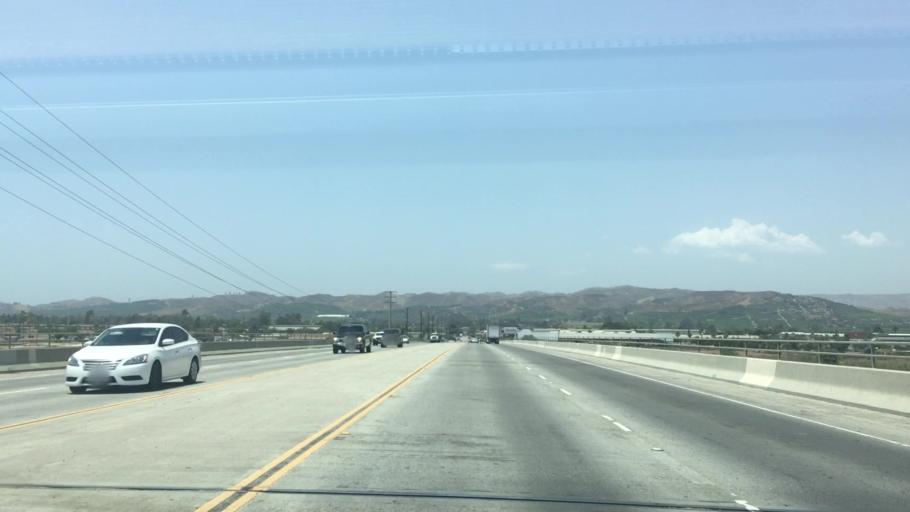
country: US
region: California
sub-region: Ventura County
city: Saticoy
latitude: 34.2768
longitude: -119.1390
